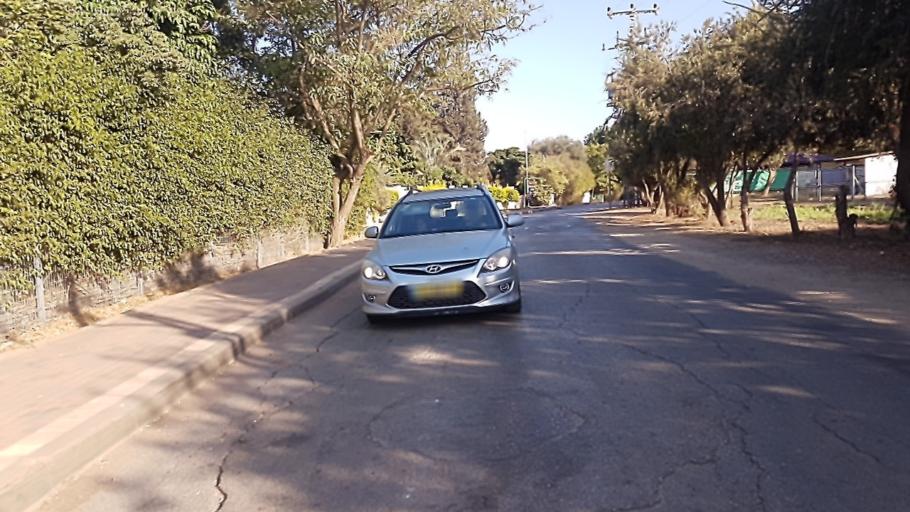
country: IL
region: Central District
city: Hod HaSharon
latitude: 32.1405
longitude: 34.9061
